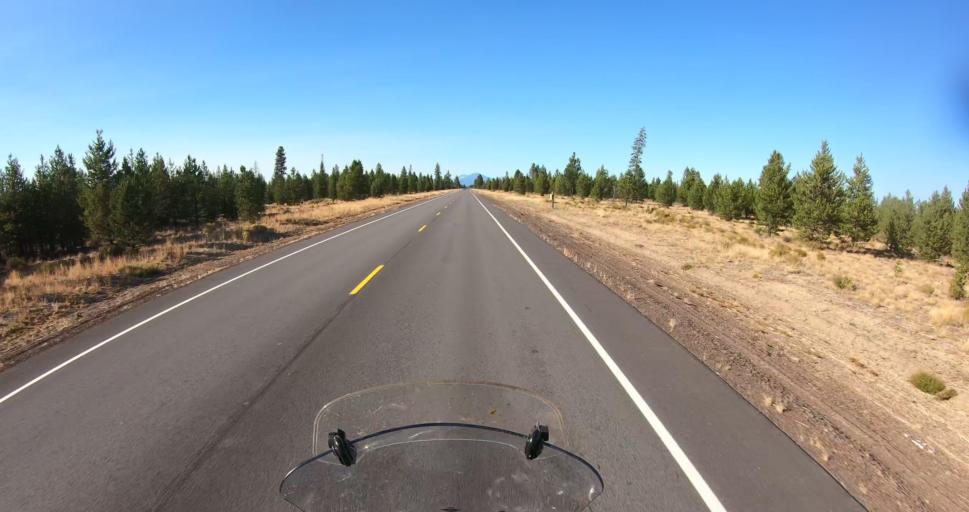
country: US
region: Oregon
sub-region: Deschutes County
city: La Pine
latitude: 43.6115
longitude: -121.5036
